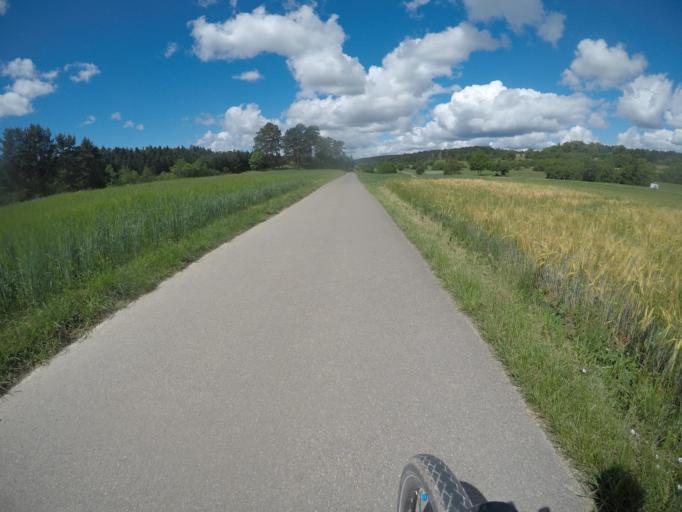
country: DE
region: Baden-Wuerttemberg
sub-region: Karlsruhe Region
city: Horb am Neckar
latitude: 48.4745
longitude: 8.7337
